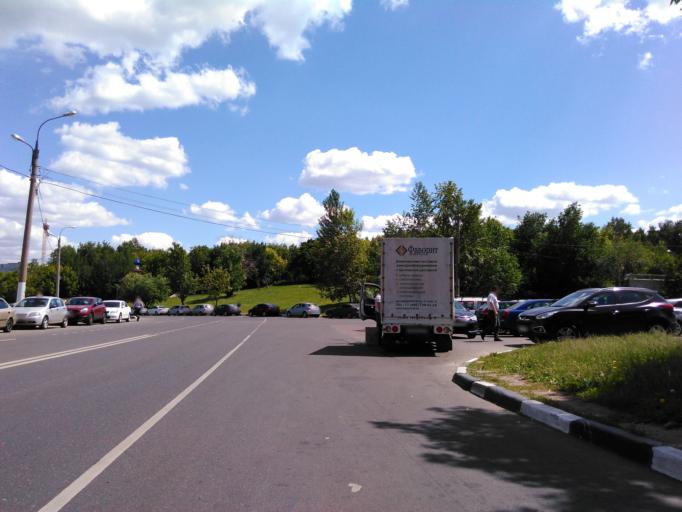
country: RU
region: Moskovskaya
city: Cheremushki
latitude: 55.6572
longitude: 37.5441
